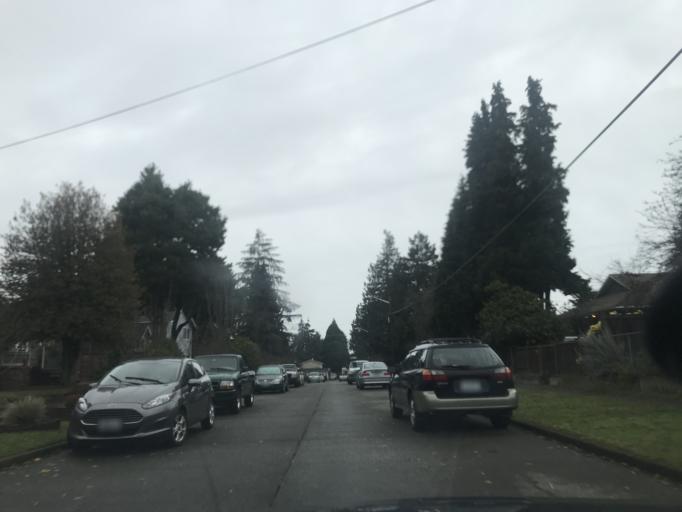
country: US
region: Washington
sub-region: King County
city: White Center
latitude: 47.5321
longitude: -122.3564
